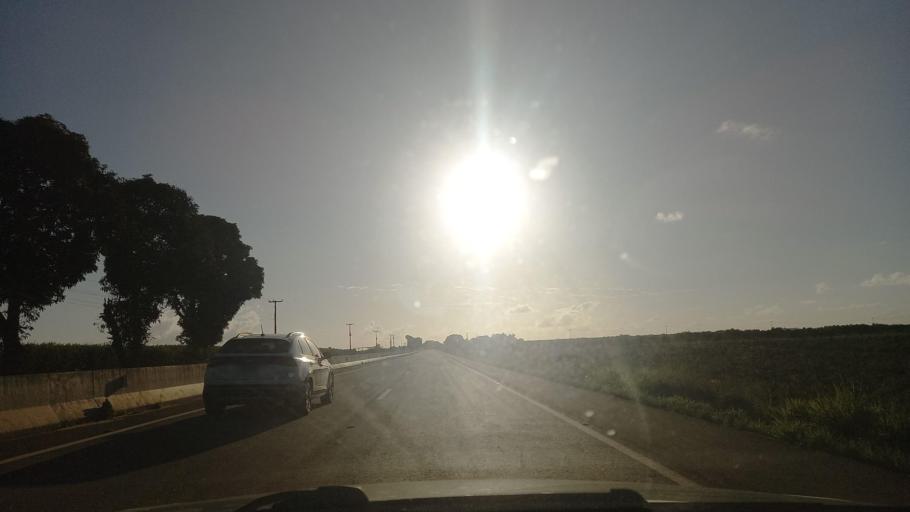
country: BR
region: Alagoas
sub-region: Campo Alegre
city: Campo Alegre
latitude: -9.7937
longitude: -36.3119
